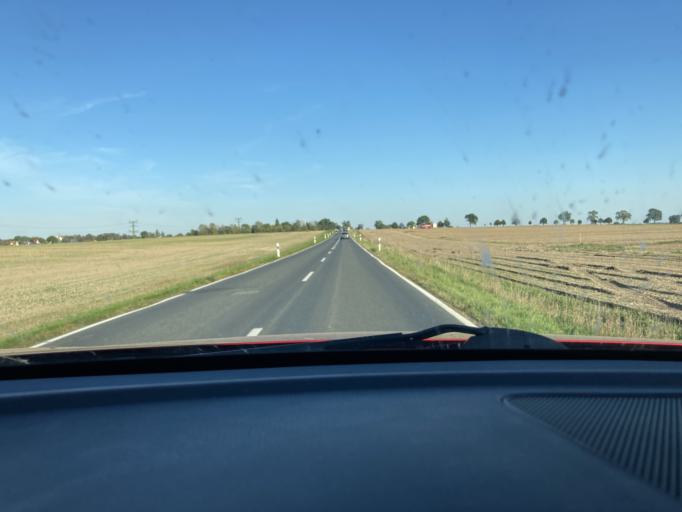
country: DE
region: Mecklenburg-Vorpommern
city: Alt-Sanitz
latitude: 53.8672
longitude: 13.5461
